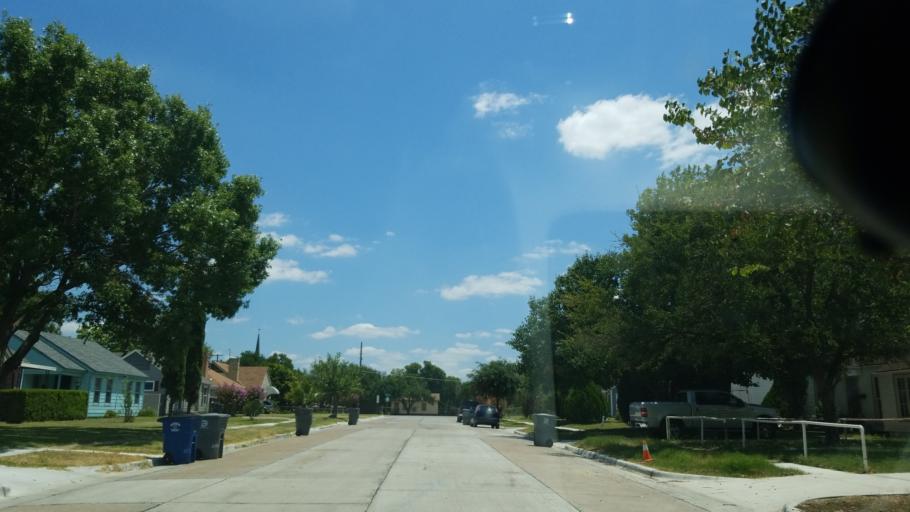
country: US
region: Texas
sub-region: Dallas County
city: Cockrell Hill
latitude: 32.7243
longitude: -96.8458
